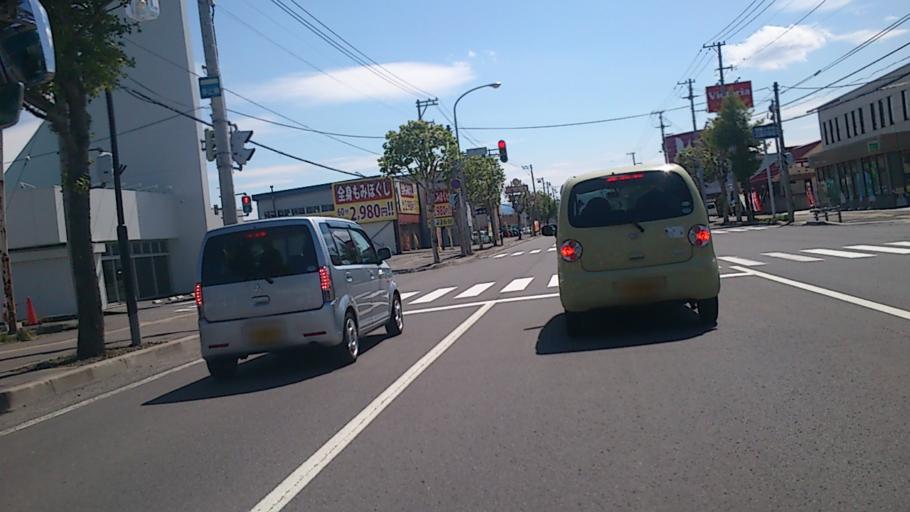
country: JP
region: Hokkaido
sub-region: Asahikawa-shi
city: Asahikawa
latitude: 43.8092
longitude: 142.3943
